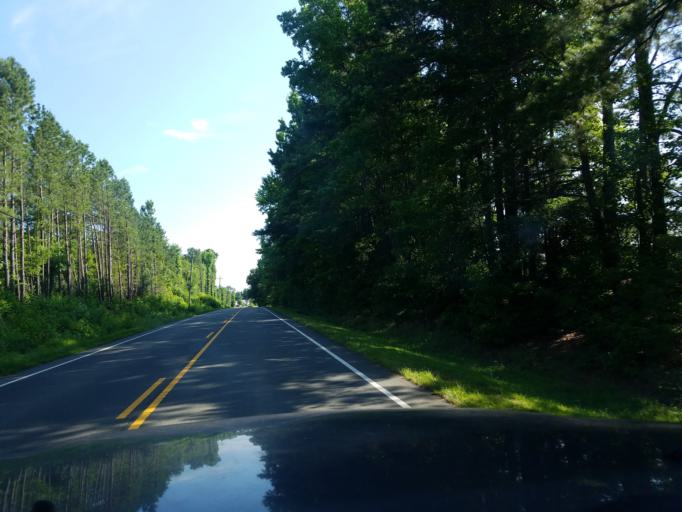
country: US
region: North Carolina
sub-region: Granville County
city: Butner
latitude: 36.2212
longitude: -78.7220
